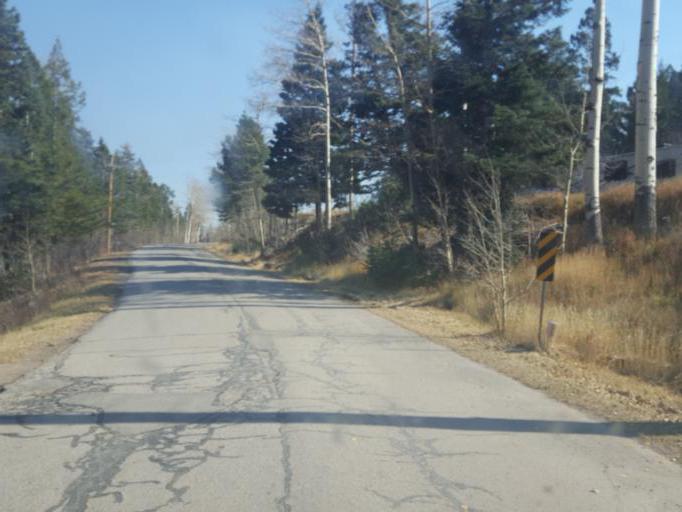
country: US
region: New Mexico
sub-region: Los Alamos County
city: Los Alamos
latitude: 35.8943
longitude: -106.3890
